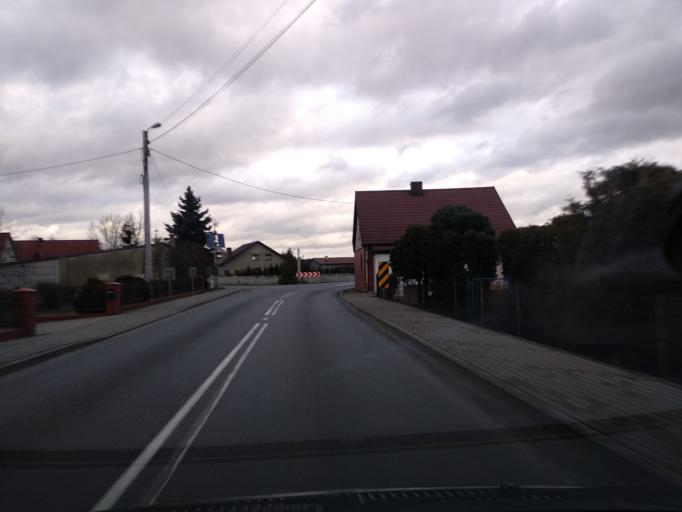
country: PL
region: Lower Silesian Voivodeship
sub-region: Powiat olesnicki
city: Miedzyborz
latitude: 51.4418
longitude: 17.7020
